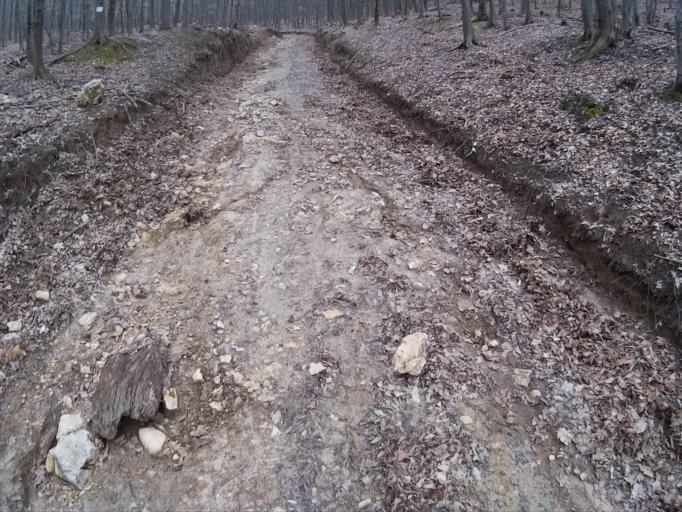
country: HU
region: Veszprem
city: Veszprem
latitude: 47.1736
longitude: 17.8712
